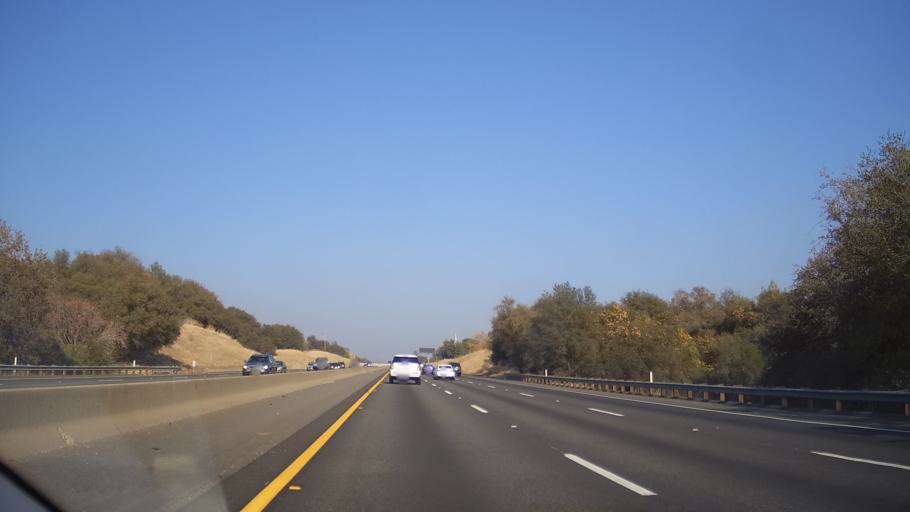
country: US
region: California
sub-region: Placer County
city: Newcastle
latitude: 38.8492
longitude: -121.1501
